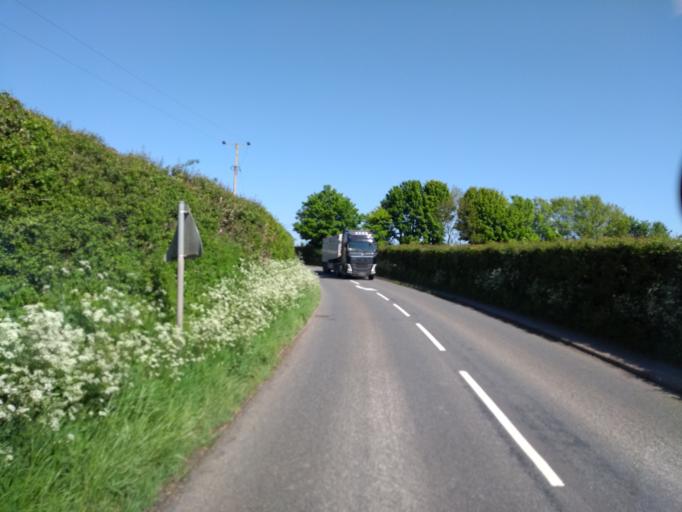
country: GB
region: England
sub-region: Somerset
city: Chard
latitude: 50.8621
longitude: -2.9596
